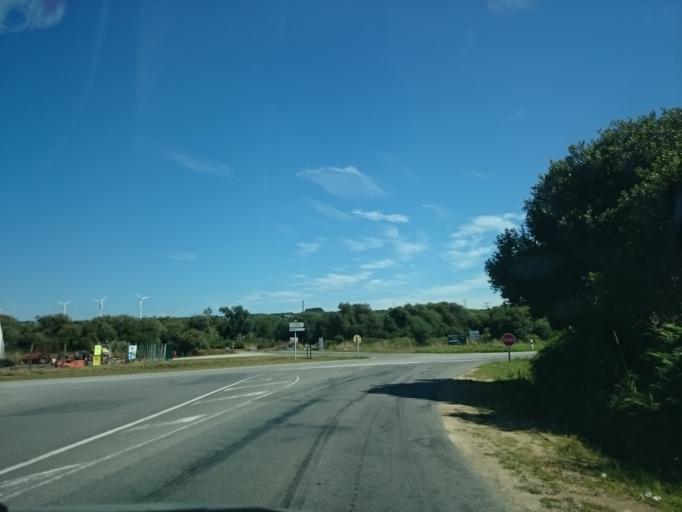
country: FR
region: Brittany
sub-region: Departement du Finistere
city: Saint-Renan
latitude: 48.4398
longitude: -4.6457
